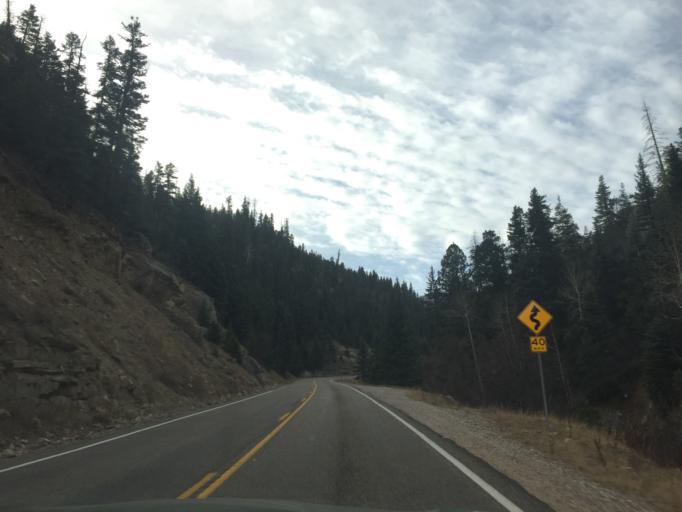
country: US
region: Utah
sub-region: Iron County
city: Cedar City
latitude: 37.6126
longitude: -112.9327
